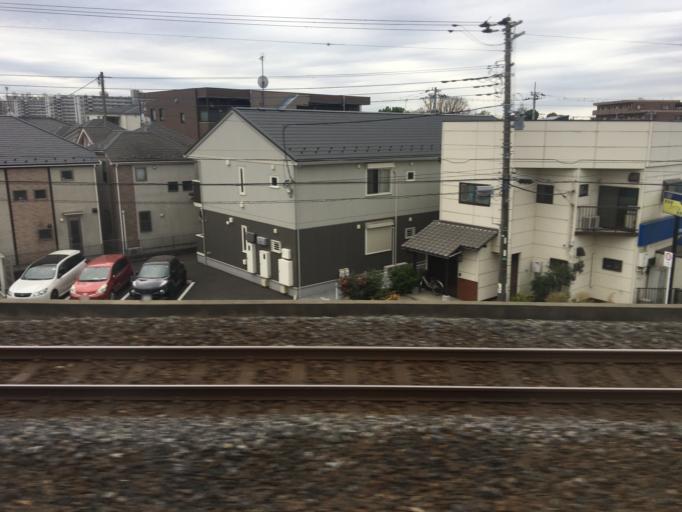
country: JP
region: Chiba
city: Nagareyama
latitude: 35.8354
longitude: 139.9065
